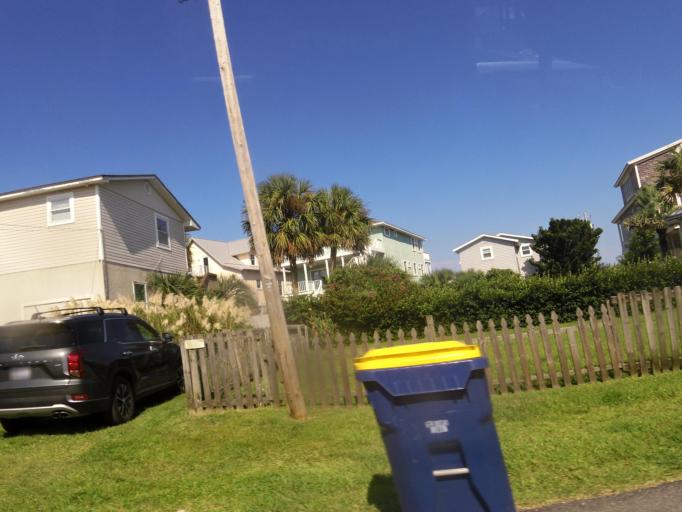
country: US
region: Florida
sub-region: Nassau County
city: Fernandina Beach
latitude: 30.6862
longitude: -81.4300
